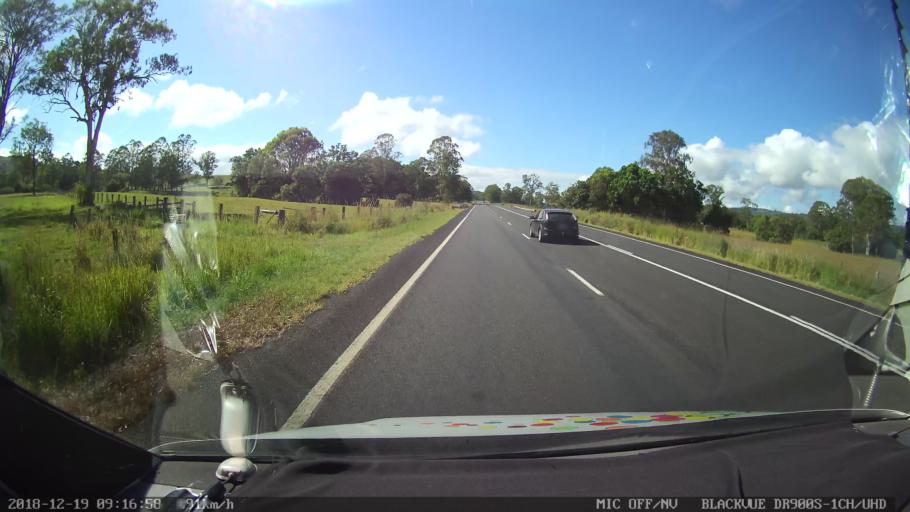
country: AU
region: New South Wales
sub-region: Kyogle
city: Kyogle
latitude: -28.5273
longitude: 152.9718
